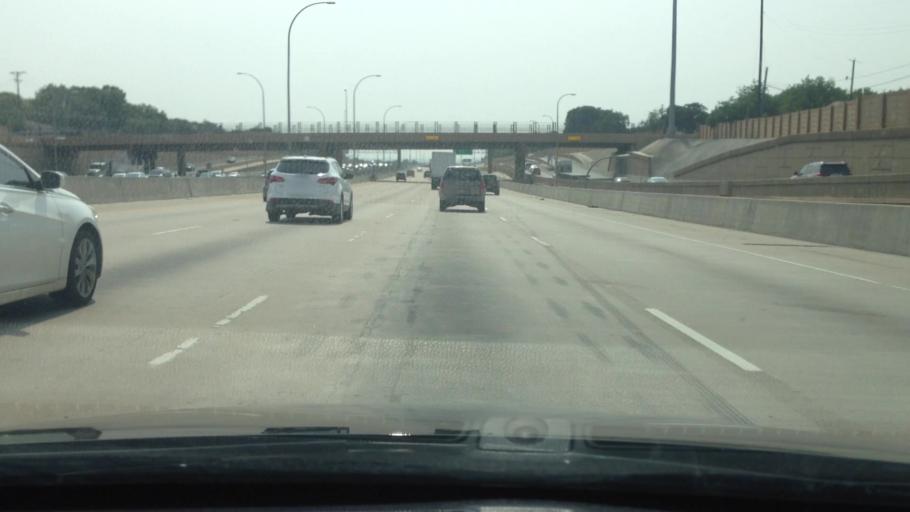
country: US
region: Texas
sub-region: Dallas County
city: Addison
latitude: 32.9229
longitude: -96.8465
